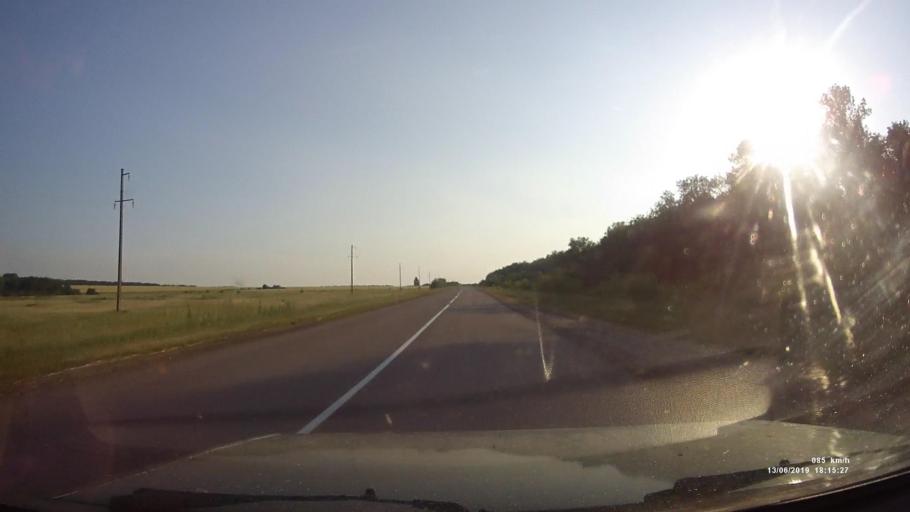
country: RU
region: Rostov
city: Kazanskaya
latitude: 49.9312
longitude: 41.3566
